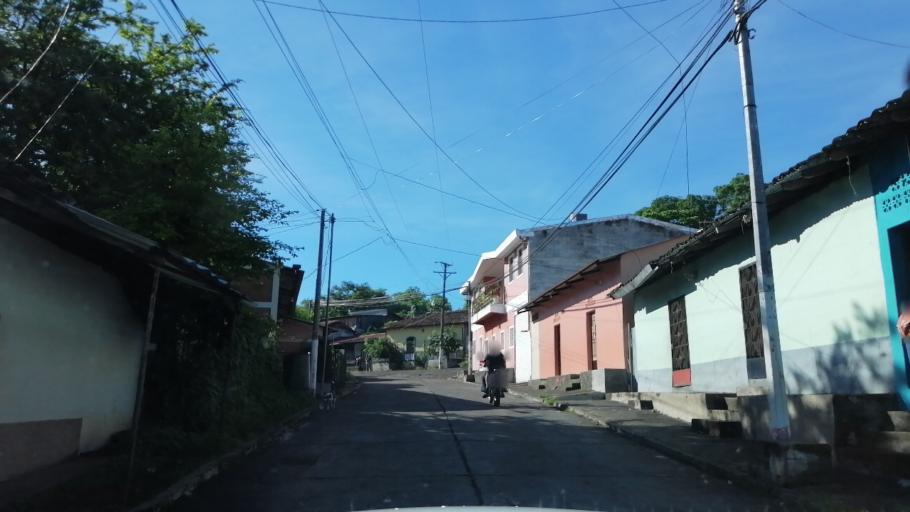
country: SV
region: Morazan
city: Cacaopera
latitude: 13.7723
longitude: -88.0776
